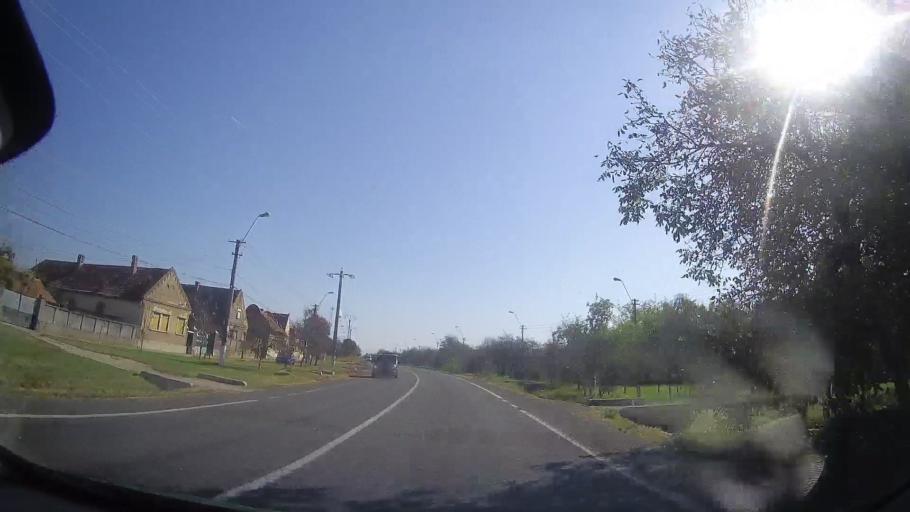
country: RO
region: Timis
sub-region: Comuna Belint
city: Belint
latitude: 45.7488
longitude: 21.7695
